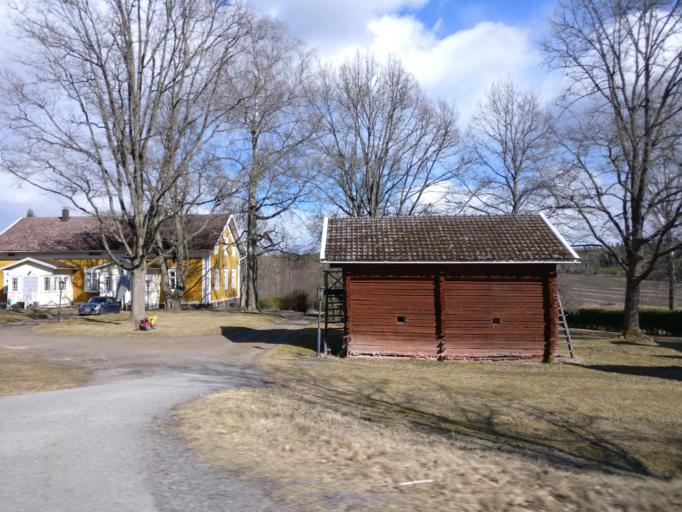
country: FI
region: Uusimaa
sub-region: Helsinki
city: Sammatti
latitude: 60.3000
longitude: 23.7570
